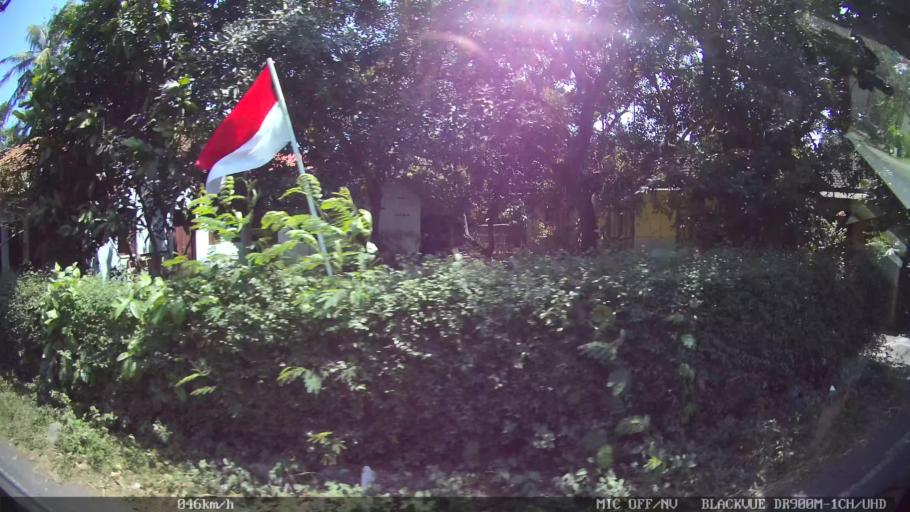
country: ID
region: Daerah Istimewa Yogyakarta
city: Srandakan
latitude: -7.9425
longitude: 110.2306
